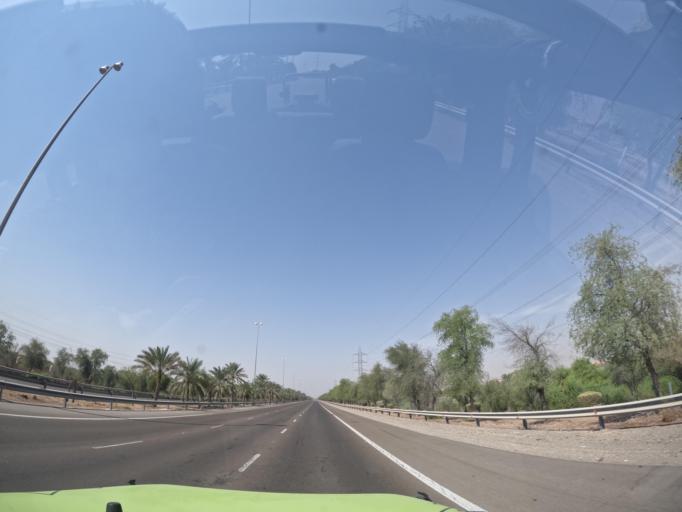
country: AE
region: Abu Dhabi
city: Al Ain
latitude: 24.2091
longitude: 55.4449
